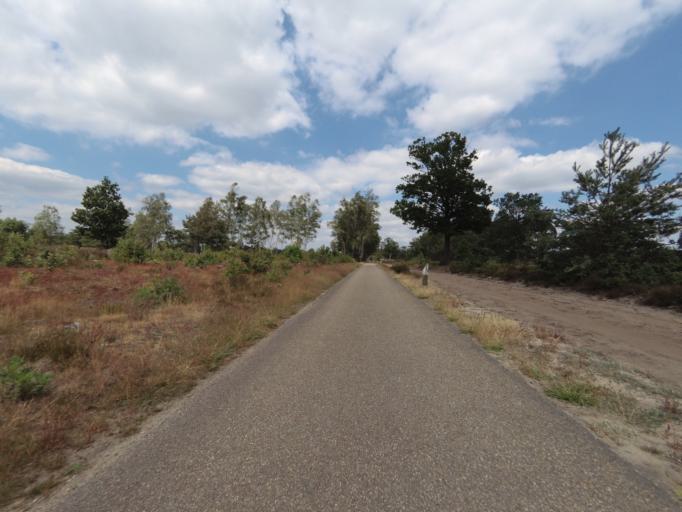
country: NL
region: Overijssel
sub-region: Gemeente Hof van Twente
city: Markelo
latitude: 52.3408
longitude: 6.4526
